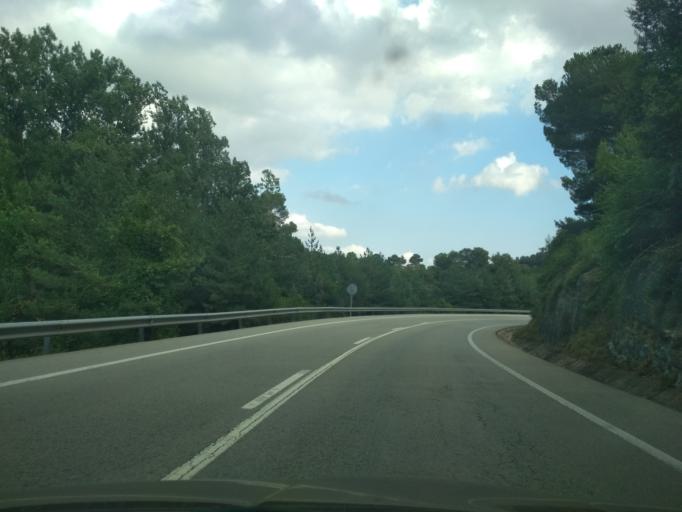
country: ES
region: Catalonia
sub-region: Provincia de Barcelona
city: Sant Feliu de Codines
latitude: 41.7092
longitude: 2.1554
